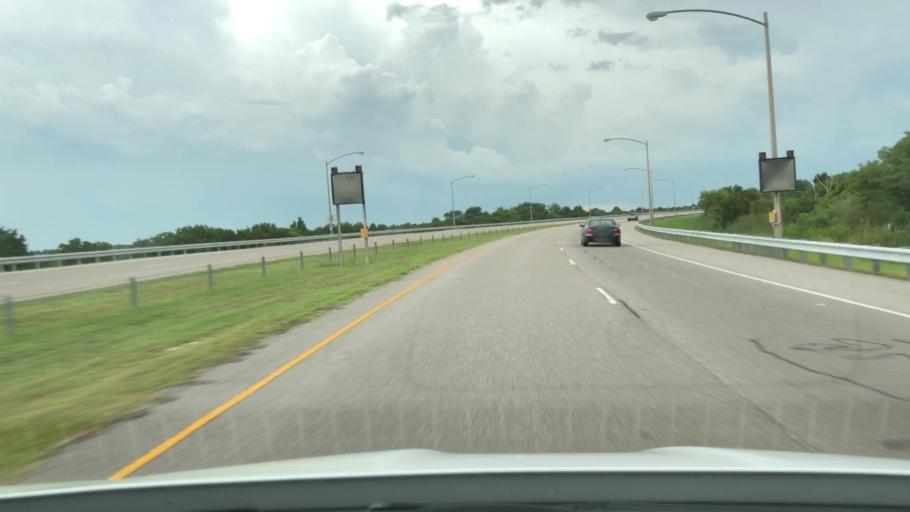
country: US
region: Virginia
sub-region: Northampton County
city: Cape Charles
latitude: 37.0968
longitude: -75.9697
